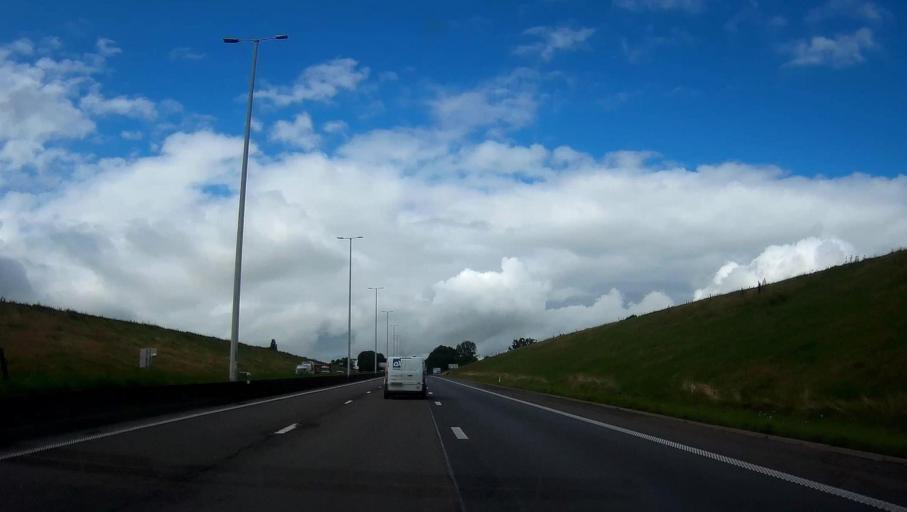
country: BE
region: Wallonia
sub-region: Province de Liege
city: Engis
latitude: 50.6145
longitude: 5.3800
